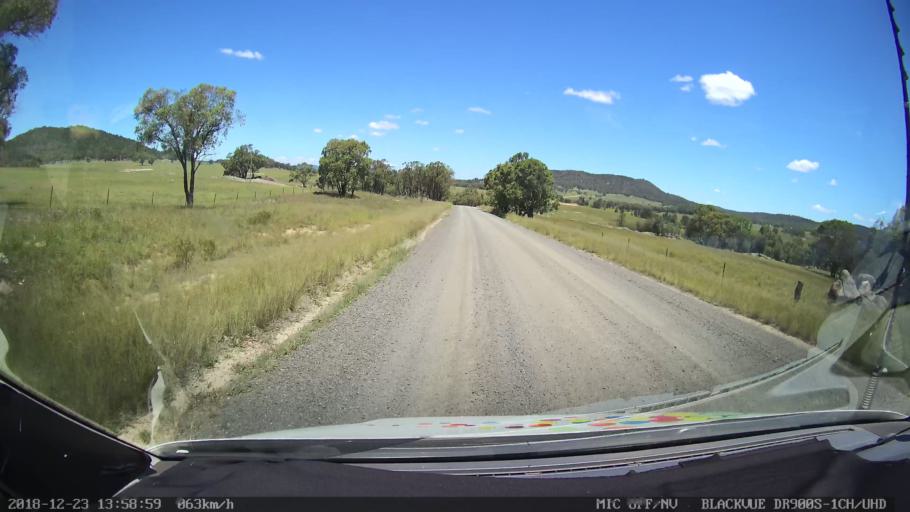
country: AU
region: New South Wales
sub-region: Tamworth Municipality
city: Manilla
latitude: -30.6037
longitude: 151.0946
